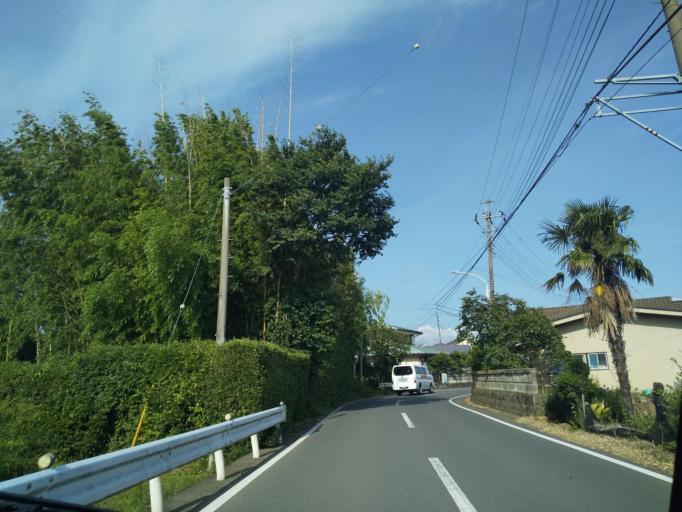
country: JP
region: Kanagawa
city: Zama
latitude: 35.4895
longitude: 139.3821
